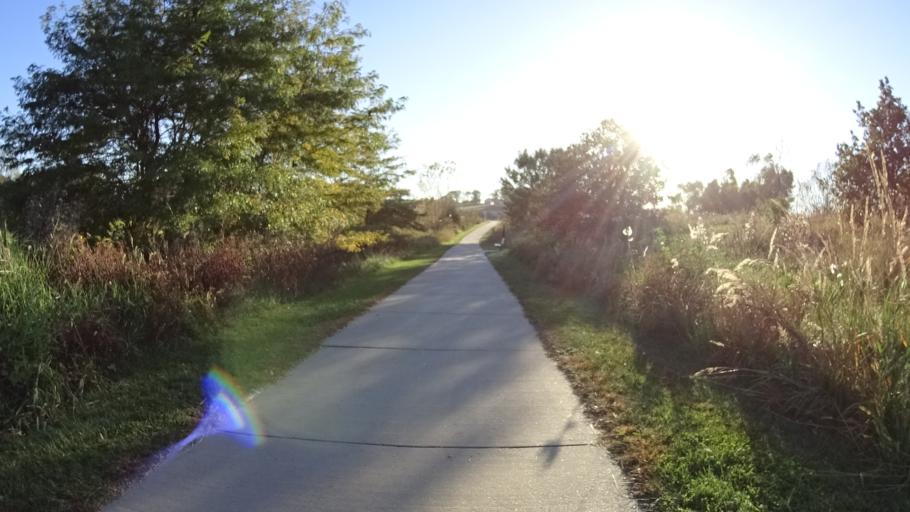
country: US
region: Nebraska
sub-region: Sarpy County
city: Papillion
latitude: 41.1363
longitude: -96.0725
